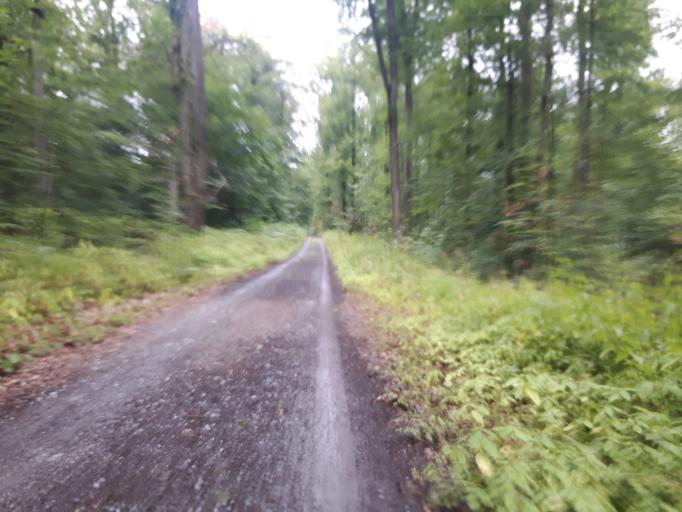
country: DE
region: Baden-Wuerttemberg
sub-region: Regierungsbezirk Stuttgart
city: Eppingen
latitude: 49.1086
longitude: 8.9450
